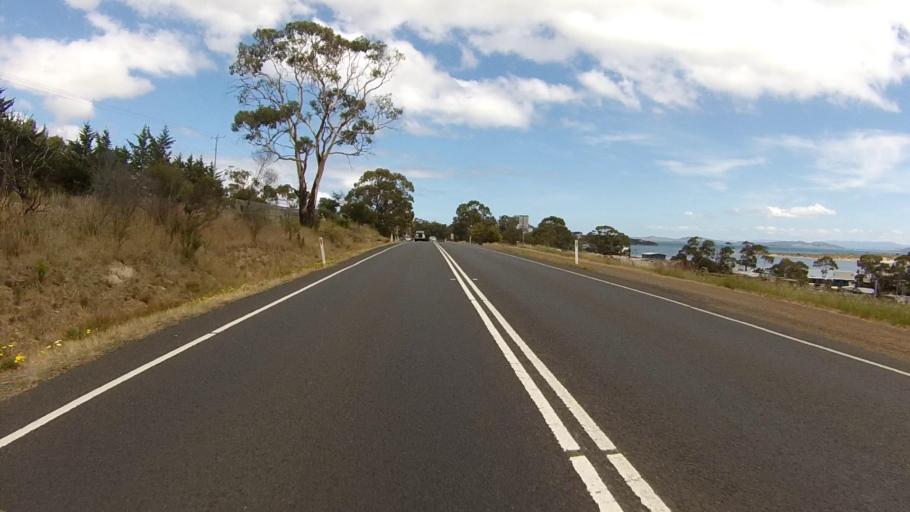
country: AU
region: Tasmania
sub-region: Sorell
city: Sorell
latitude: -42.8383
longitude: 147.6229
